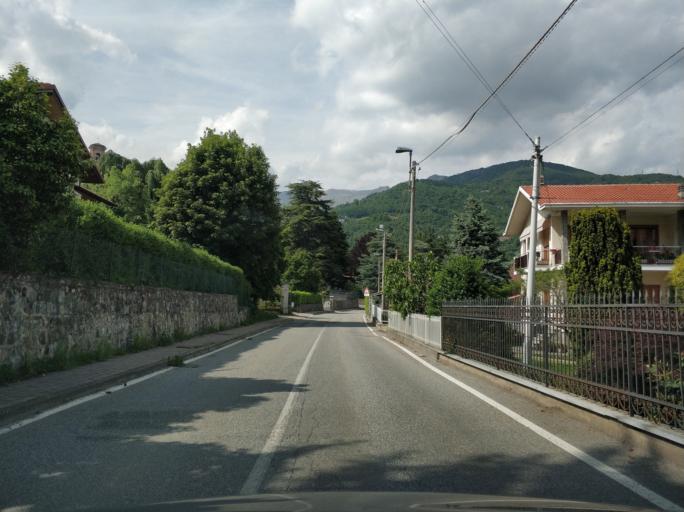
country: IT
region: Piedmont
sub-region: Provincia di Torino
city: Corio
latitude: 45.3112
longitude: 7.5351
